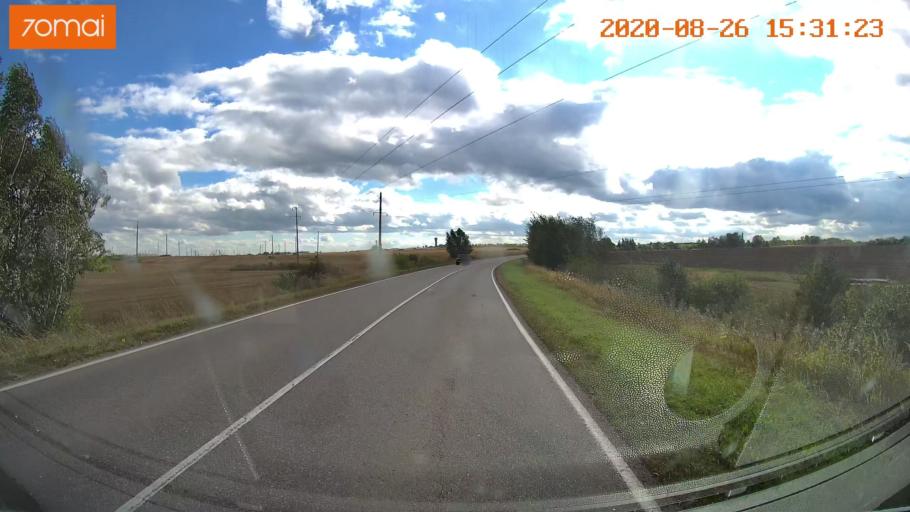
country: RU
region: Tula
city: Severo-Zadonsk
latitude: 54.0800
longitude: 38.3874
